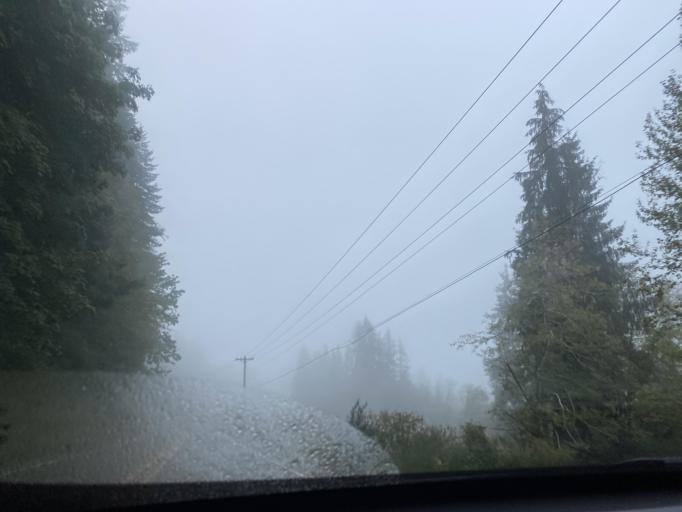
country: US
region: Washington
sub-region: Clallam County
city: Forks
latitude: 47.9296
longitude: -124.4097
